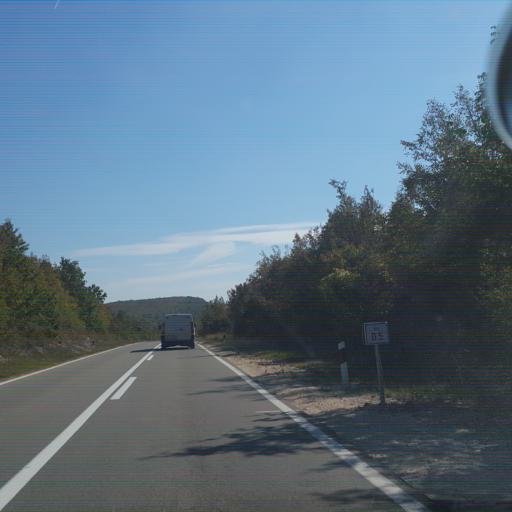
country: RS
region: Central Serbia
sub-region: Zajecarski Okrug
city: Knjazevac
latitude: 43.4991
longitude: 22.2179
